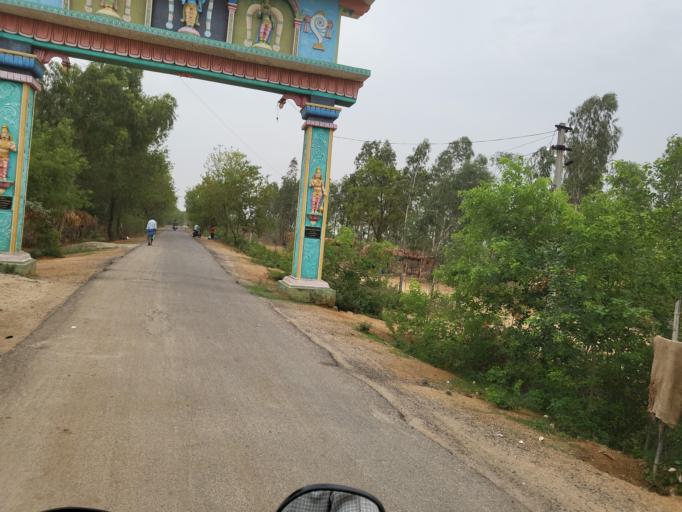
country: IN
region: Telangana
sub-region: Medak
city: Narsingi
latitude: 18.1234
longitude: 78.4922
